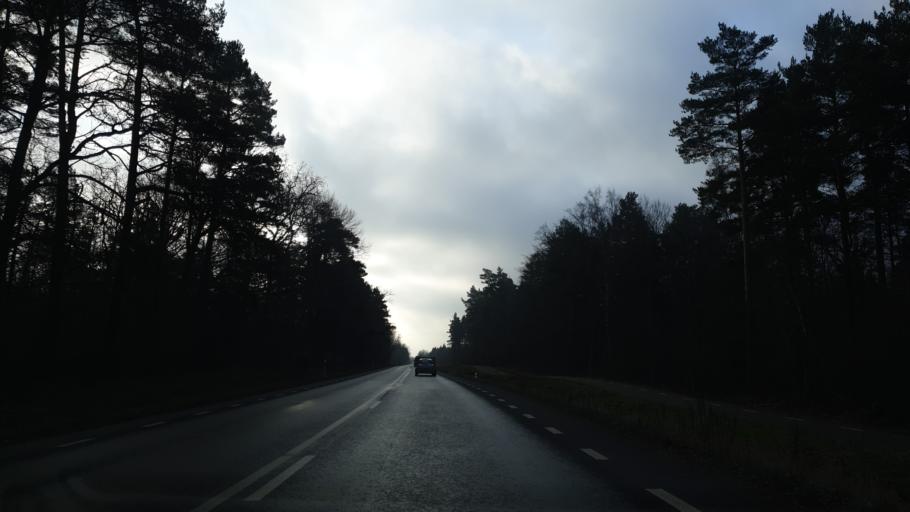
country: SE
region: Blekinge
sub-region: Karlshamns Kommun
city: Morrum
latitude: 56.1469
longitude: 14.6685
